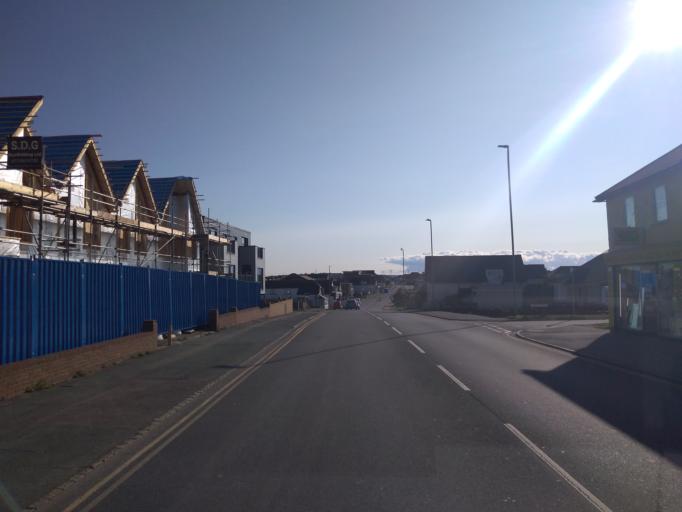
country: GB
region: England
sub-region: East Sussex
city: Peacehaven
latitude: 50.7936
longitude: -0.0116
